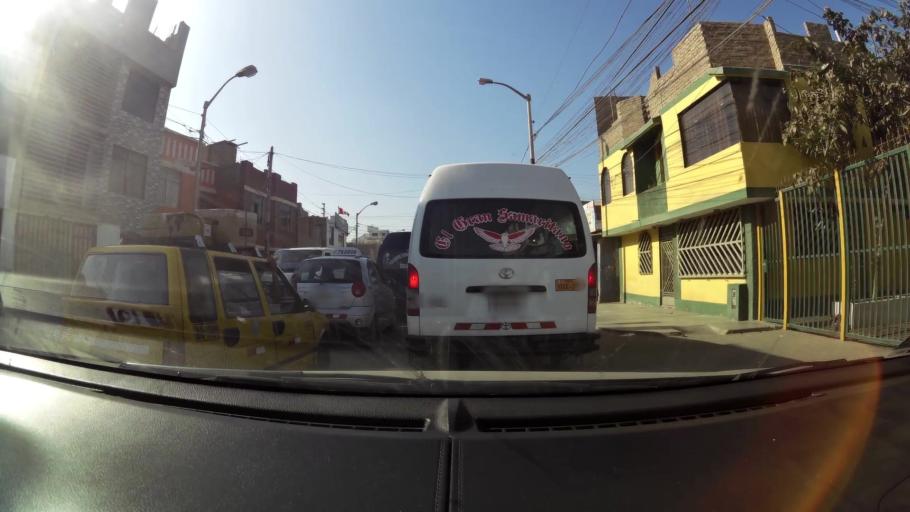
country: PE
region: Lambayeque
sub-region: Provincia de Chiclayo
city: Chiclayo
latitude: -6.7633
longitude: -79.8442
